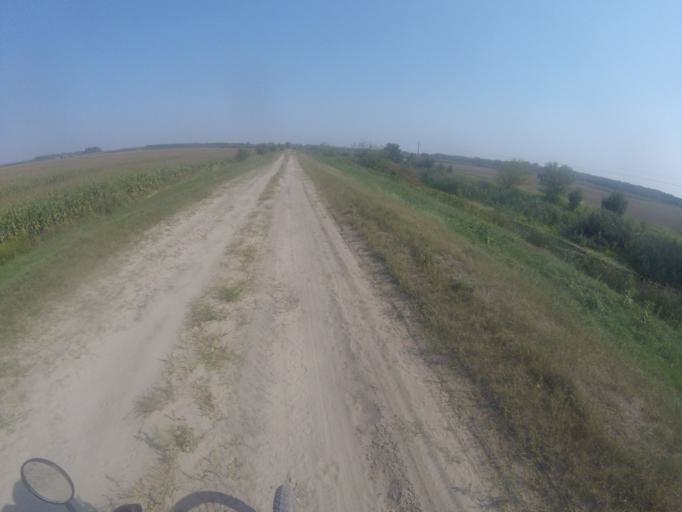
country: HU
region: Bacs-Kiskun
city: Ersekcsanad
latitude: 46.2262
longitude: 18.9596
